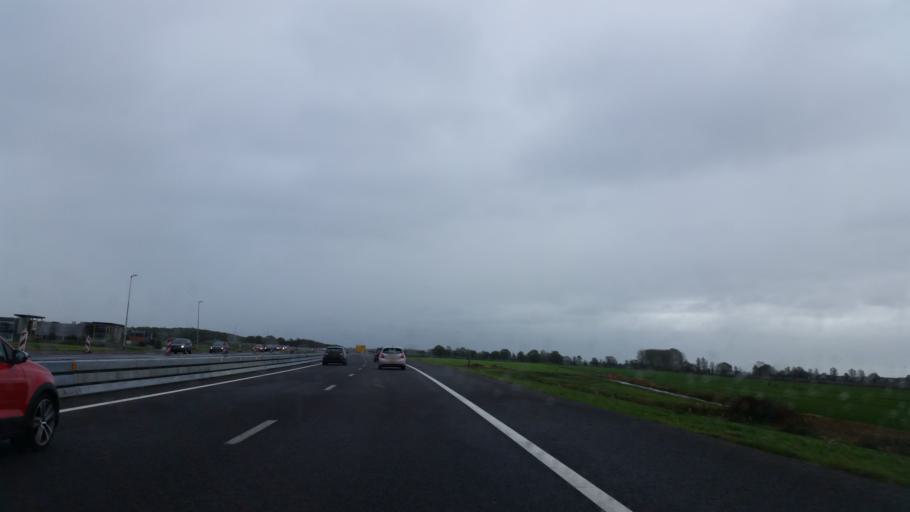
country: NL
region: Friesland
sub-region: Gemeente Skarsterlan
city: Joure
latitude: 52.9571
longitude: 5.7775
